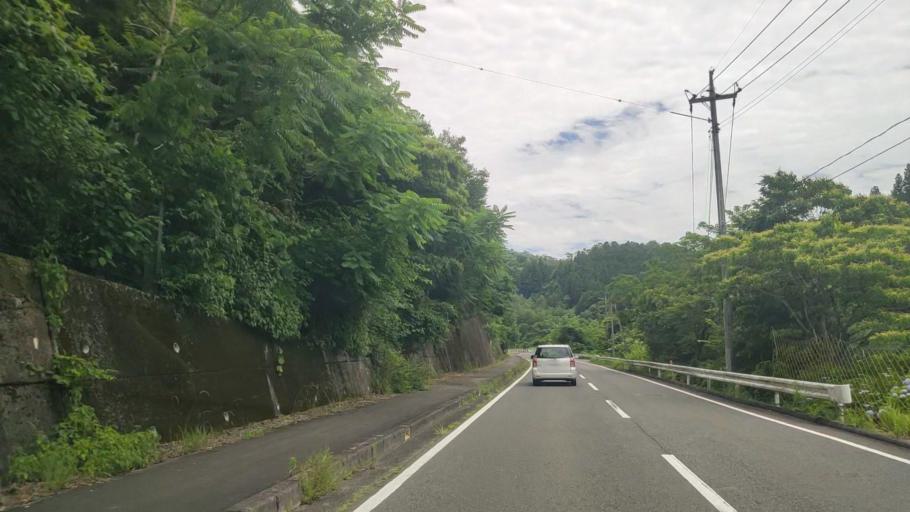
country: JP
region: Hyogo
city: Yamazakicho-nakabirose
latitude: 35.1066
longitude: 134.3024
